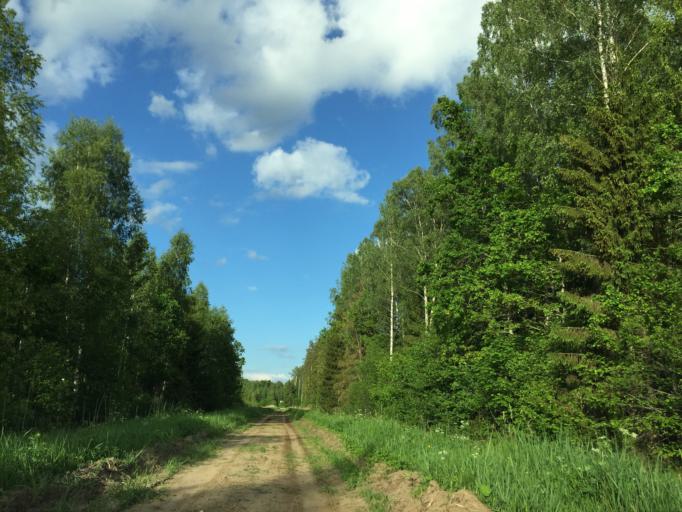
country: LV
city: Tireli
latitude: 56.7794
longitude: 23.4235
